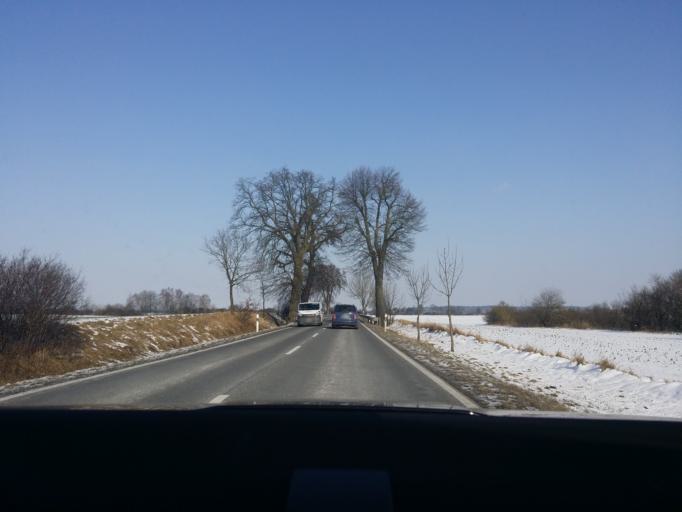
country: DE
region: Mecklenburg-Vorpommern
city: Wulkenzin
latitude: 53.5349
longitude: 13.1458
